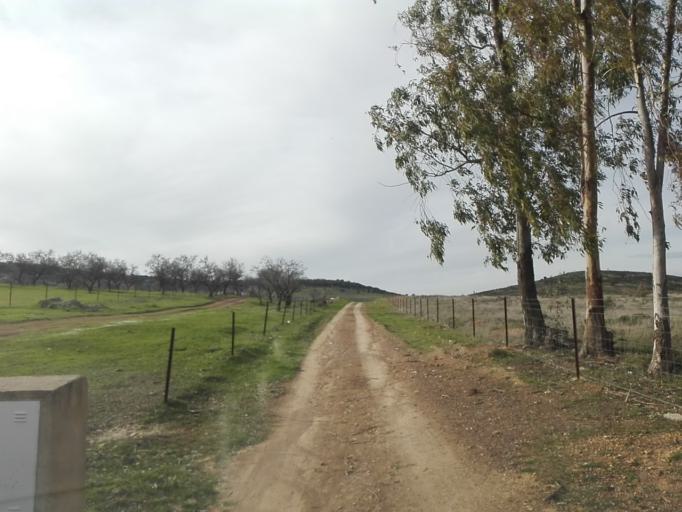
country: ES
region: Extremadura
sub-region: Provincia de Badajoz
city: Llerena
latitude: 38.2182
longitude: -6.0340
